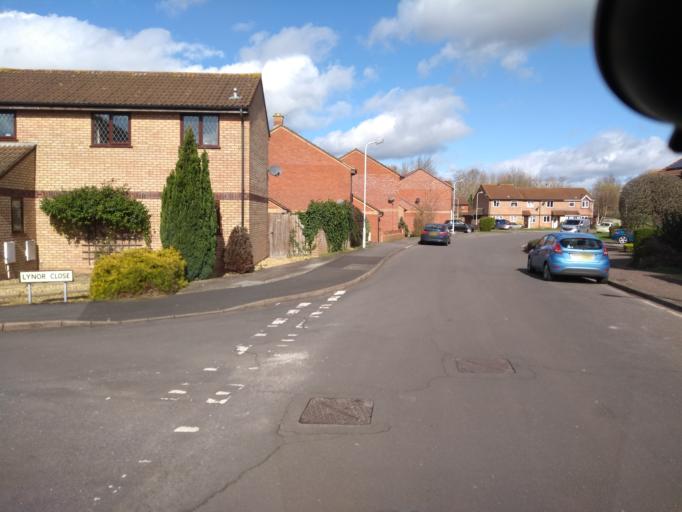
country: GB
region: England
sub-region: Somerset
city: Taunton
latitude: 51.0128
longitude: -3.0725
